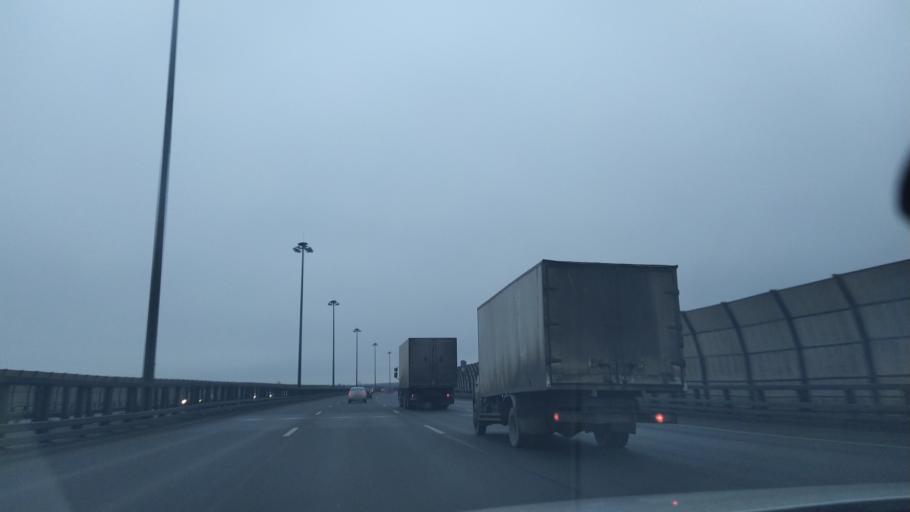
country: RU
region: St.-Petersburg
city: Krasnogvargeisky
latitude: 59.9806
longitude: 30.5199
